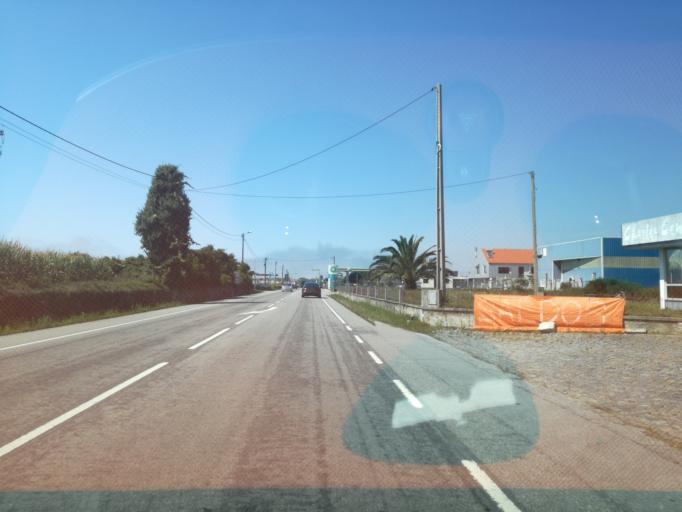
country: PT
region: Braga
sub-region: Esposende
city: Apulia
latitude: 41.5029
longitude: -8.7613
